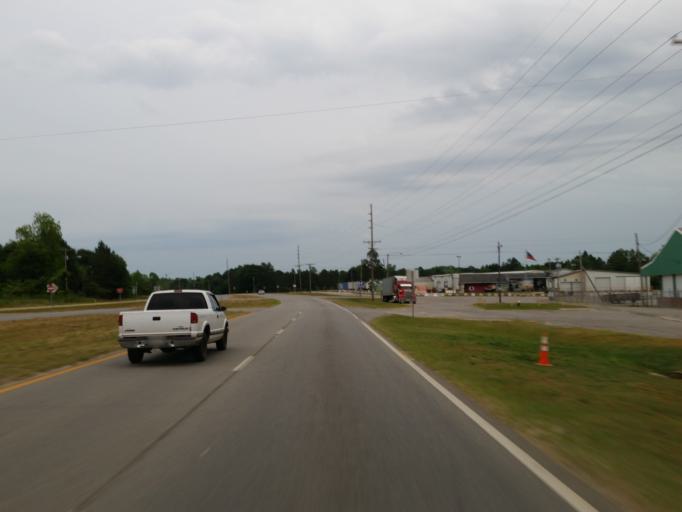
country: US
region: Georgia
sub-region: Crisp County
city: Cordele
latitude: 31.9890
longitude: -83.7932
